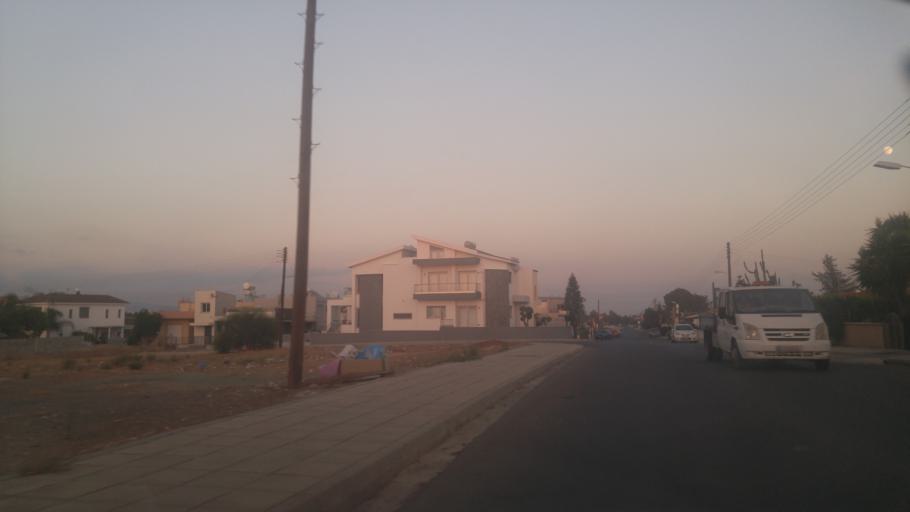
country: CY
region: Larnaka
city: Kolossi
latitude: 34.6608
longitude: 32.9597
